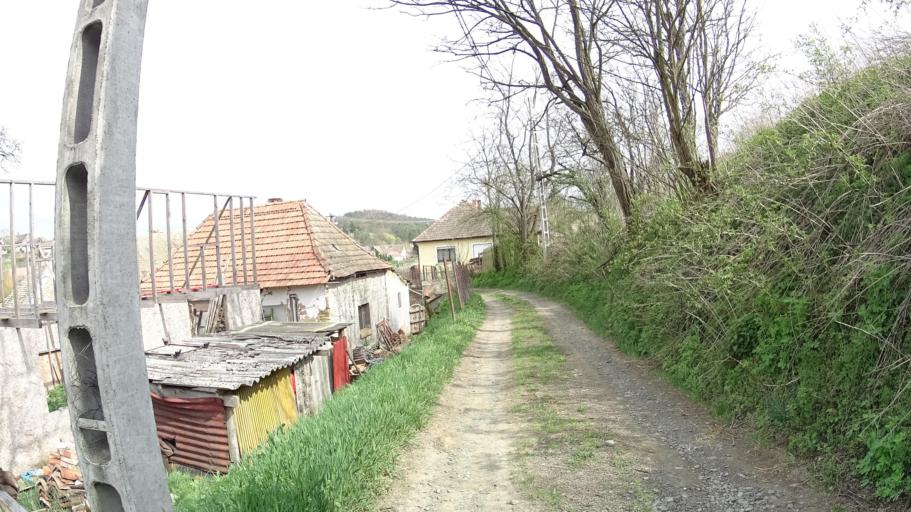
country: HU
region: Nograd
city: Diosjeno
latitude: 47.8876
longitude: 19.0669
